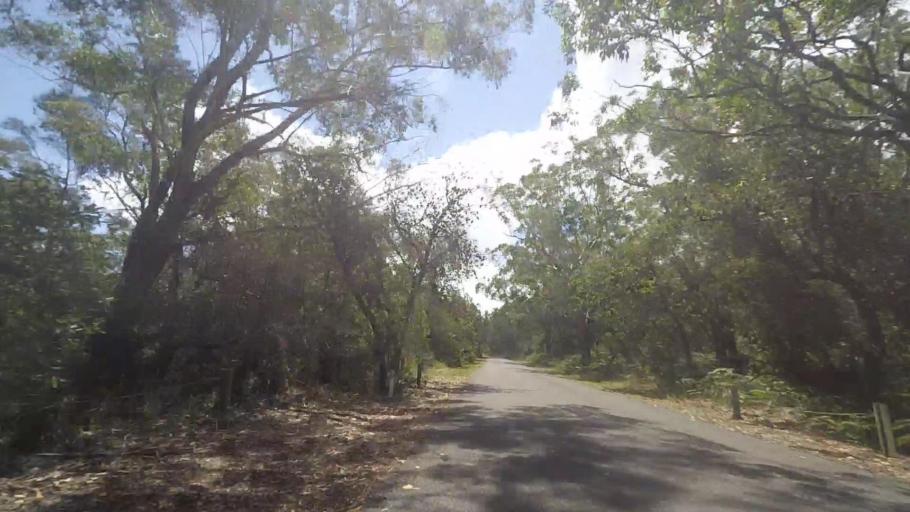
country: AU
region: New South Wales
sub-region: Great Lakes
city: Bulahdelah
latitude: -32.5069
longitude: 152.3160
